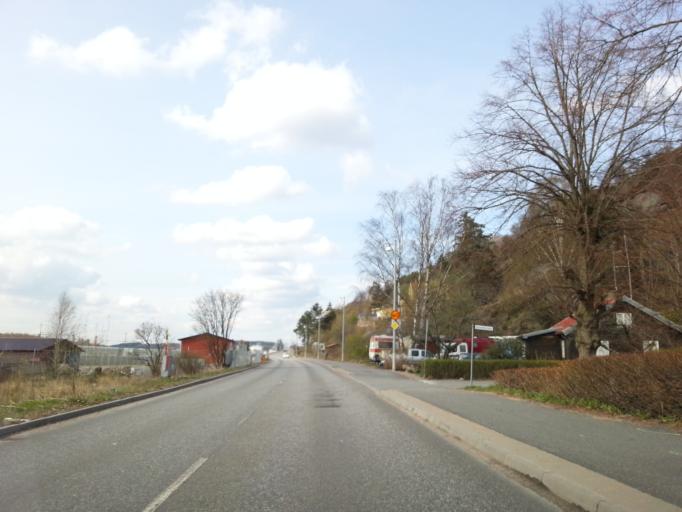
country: SE
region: Vaestra Goetaland
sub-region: Ale Kommun
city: Surte
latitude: 57.8387
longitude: 12.0146
